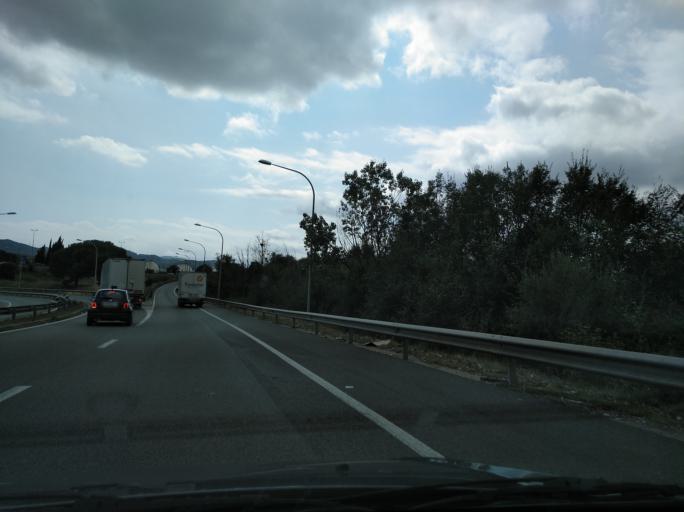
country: ES
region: Catalonia
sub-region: Provincia de Barcelona
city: Montornes del Valles
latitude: 41.5687
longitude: 2.2792
